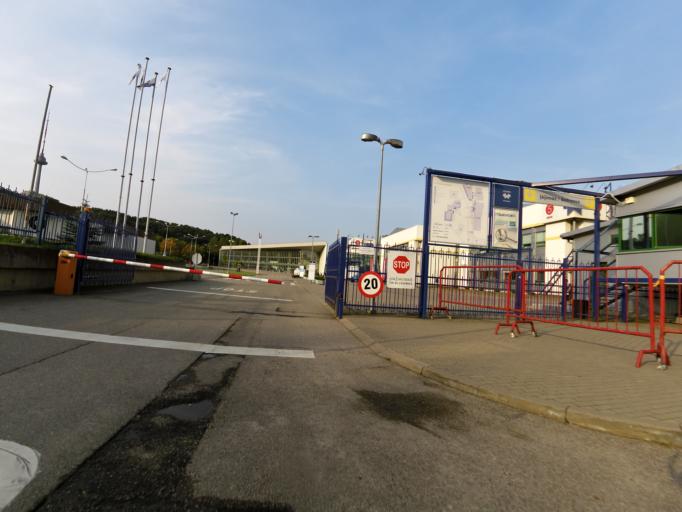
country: LT
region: Vilnius County
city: Lazdynai
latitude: 54.6779
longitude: 25.2255
